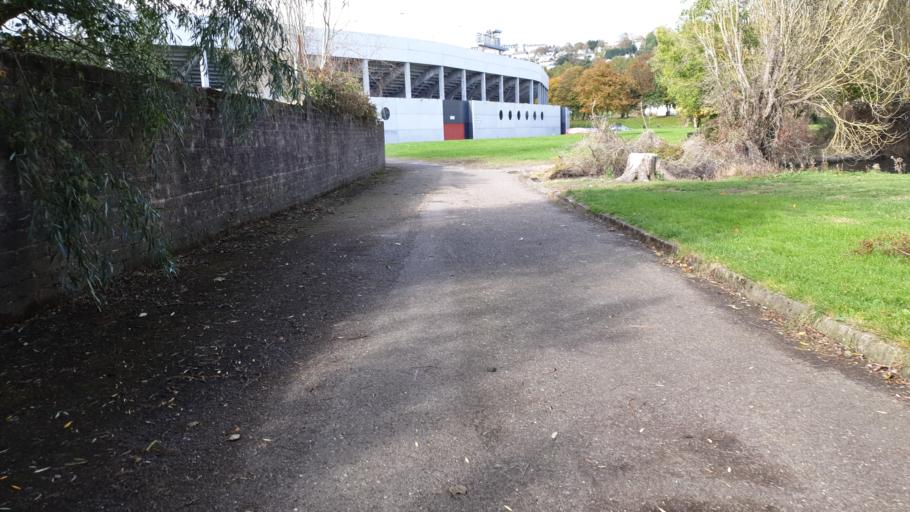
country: IE
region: Munster
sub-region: County Cork
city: Cork
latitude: 51.8993
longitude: -8.4325
